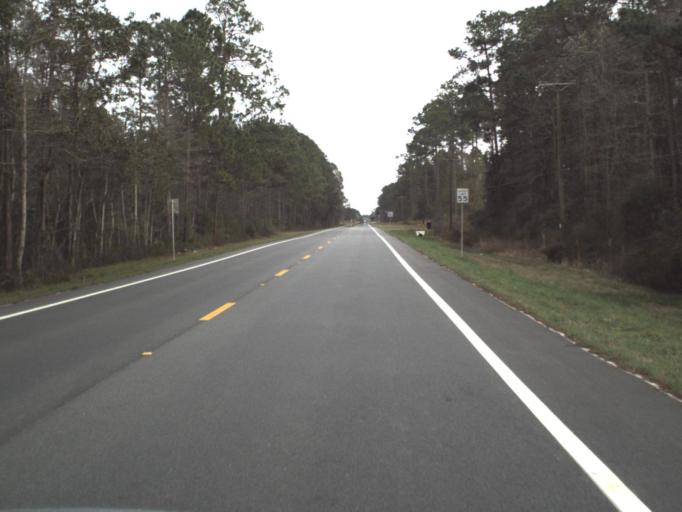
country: US
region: Florida
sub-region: Gulf County
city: Wewahitchka
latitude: 30.1351
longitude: -85.2399
